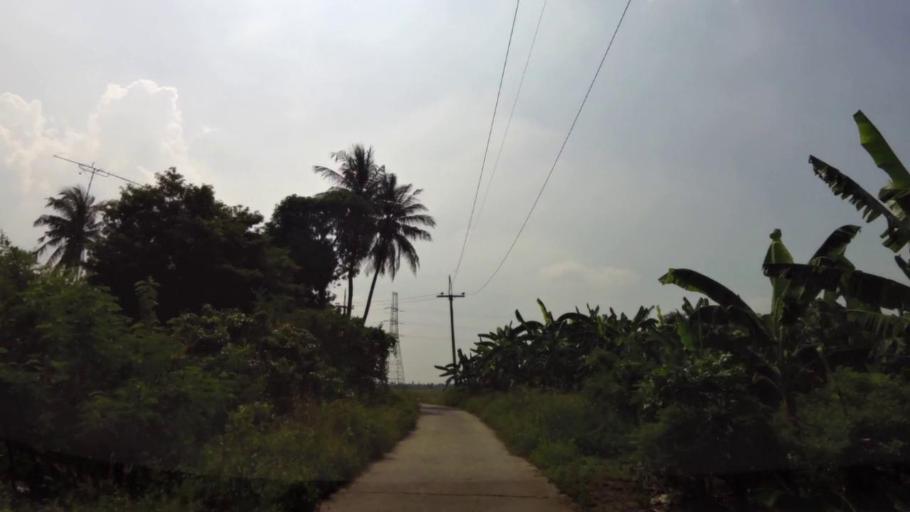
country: TH
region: Ang Thong
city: Pho Thong
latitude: 14.6235
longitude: 100.3959
